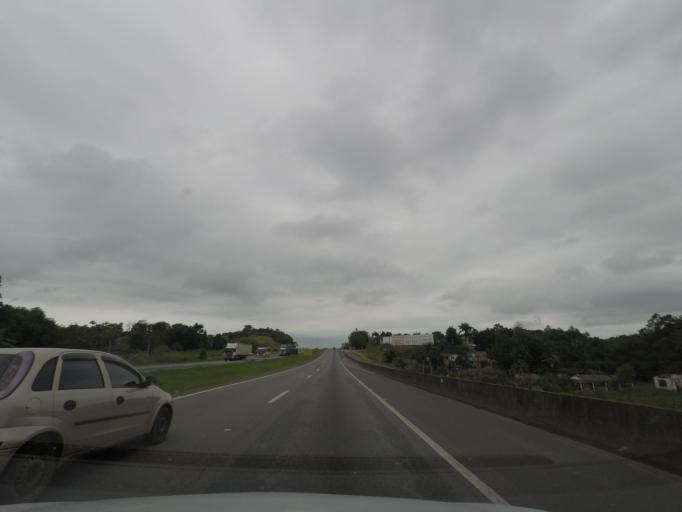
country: BR
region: Sao Paulo
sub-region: Registro
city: Registro
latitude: -24.4636
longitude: -47.8188
